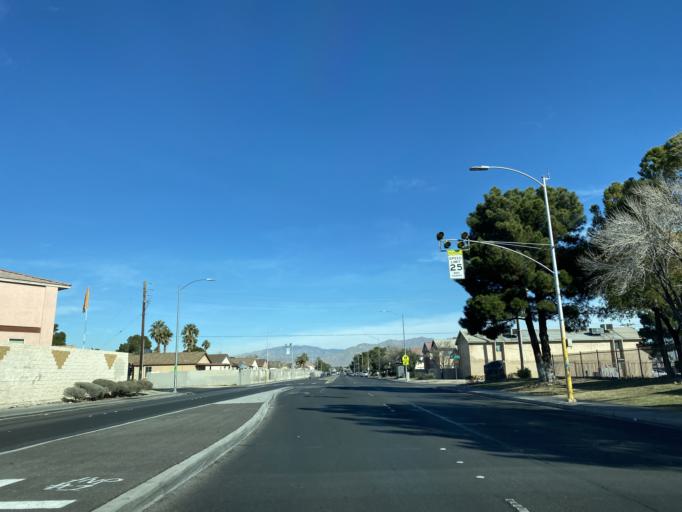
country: US
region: Nevada
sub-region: Clark County
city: Las Vegas
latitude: 36.1982
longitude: -115.2238
